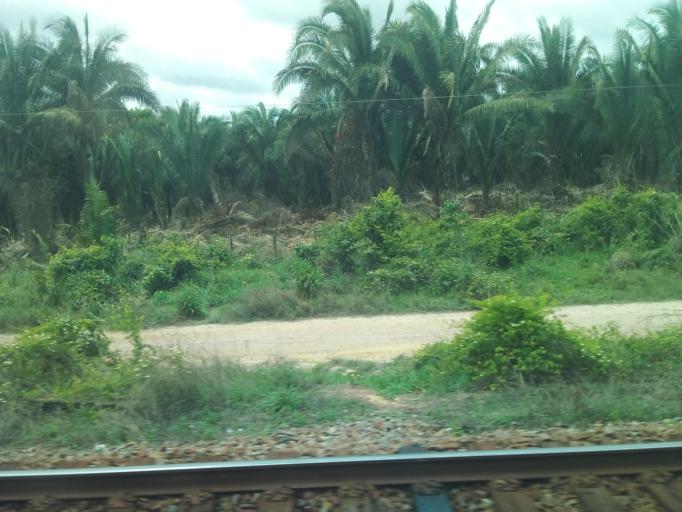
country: BR
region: Maranhao
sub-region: Santa Ines
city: Santa Ines
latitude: -3.6535
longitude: -45.8191
